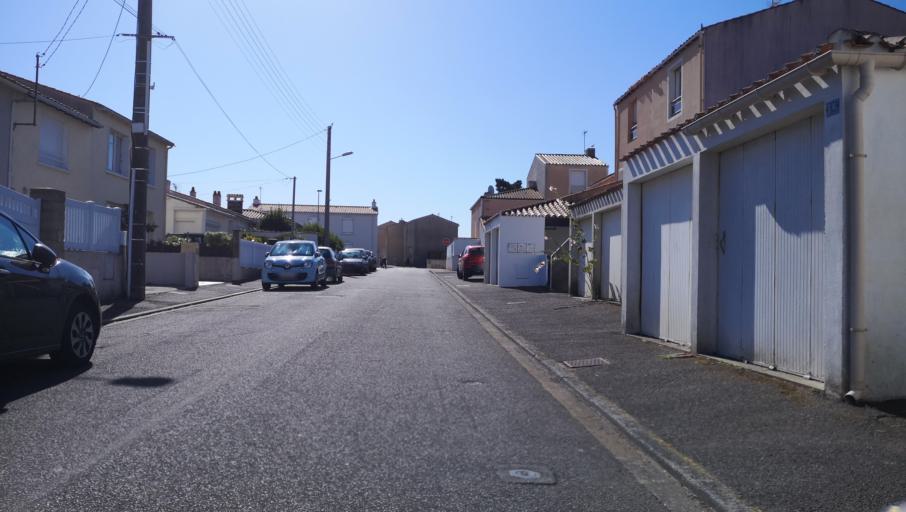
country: FR
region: Pays de la Loire
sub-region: Departement de la Vendee
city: Les Sables-d'Olonne
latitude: 46.4900
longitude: -1.7615
